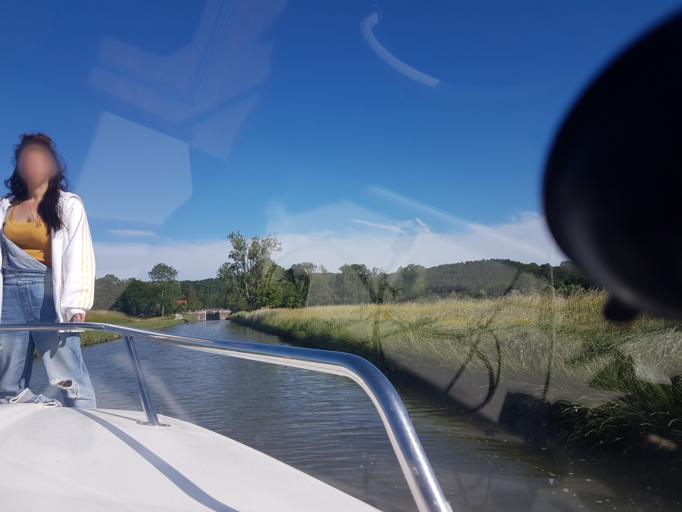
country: FR
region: Bourgogne
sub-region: Departement de la Nievre
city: Clamecy
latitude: 47.5371
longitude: 3.6090
